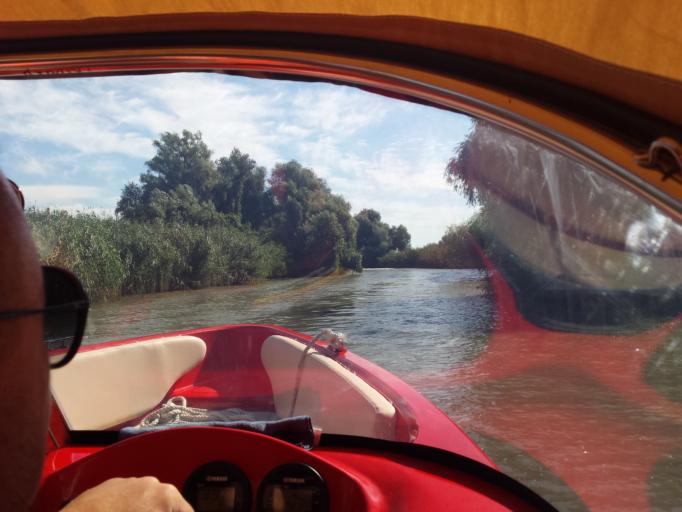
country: RO
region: Tulcea
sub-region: Comuna Pardina
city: Pardina
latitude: 45.2419
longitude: 29.0103
